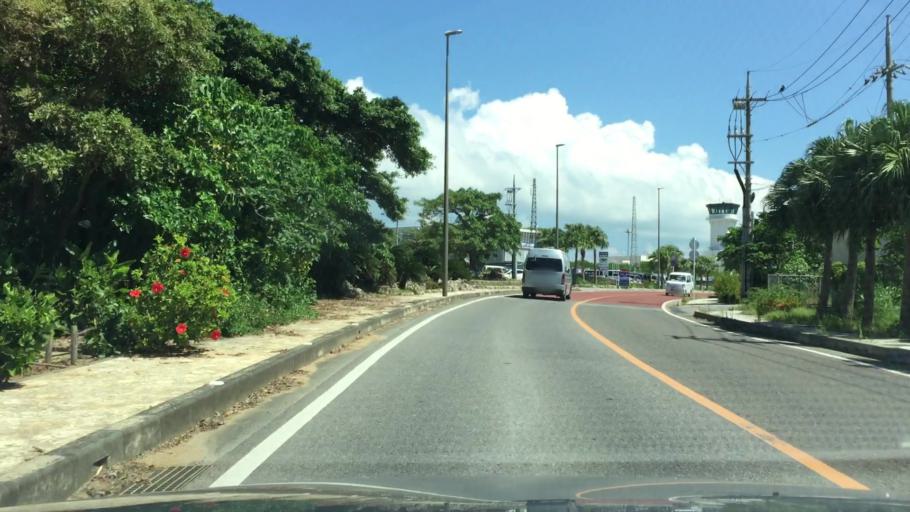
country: JP
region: Okinawa
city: Ishigaki
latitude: 24.3861
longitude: 124.2441
